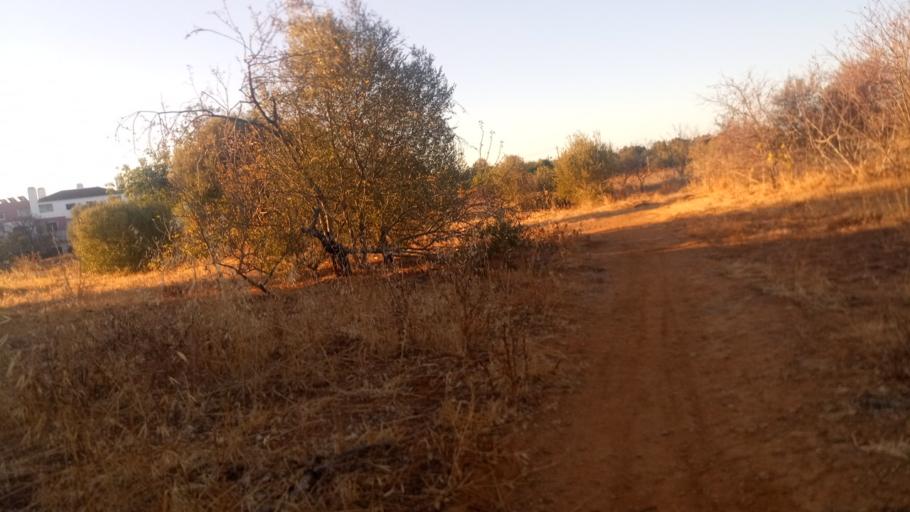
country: PT
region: Faro
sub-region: Tavira
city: Tavira
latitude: 37.1433
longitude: -7.6086
